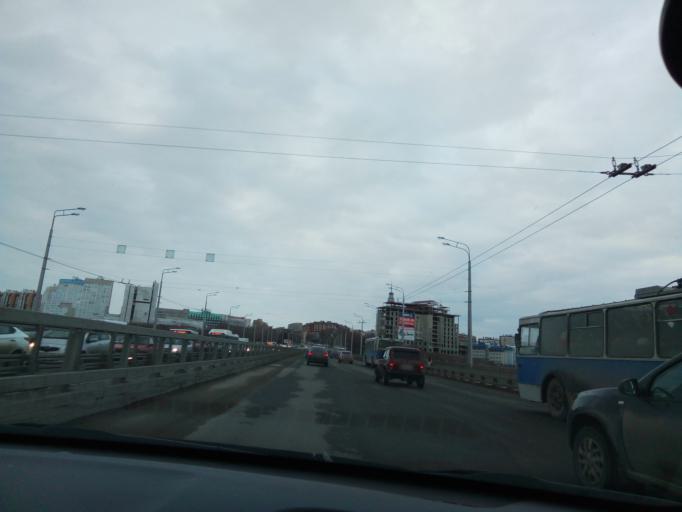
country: RU
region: Chuvashia
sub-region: Cheboksarskiy Rayon
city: Cheboksary
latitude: 56.1443
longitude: 47.2454
